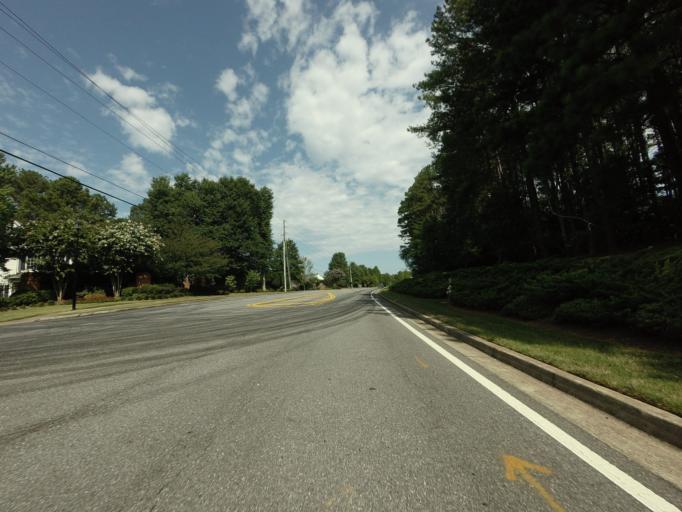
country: US
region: Georgia
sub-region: Fulton County
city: Johns Creek
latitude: 34.0435
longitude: -84.1654
